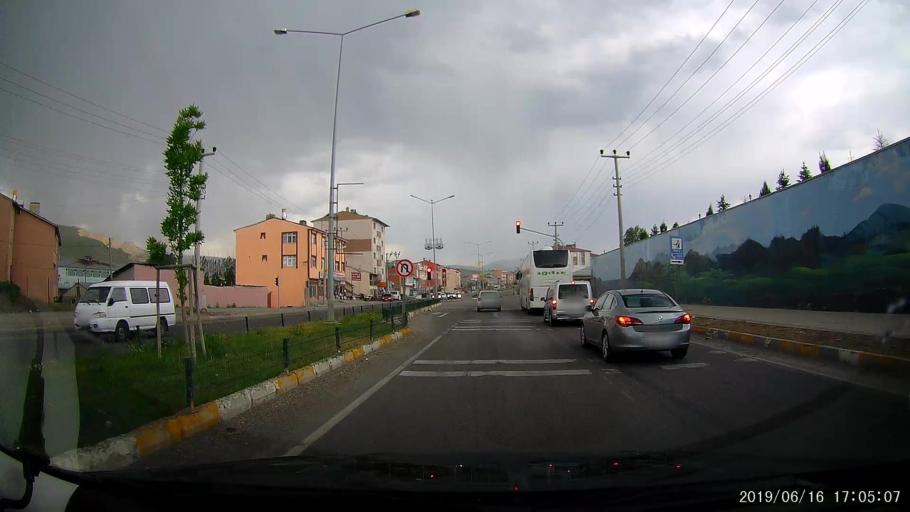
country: TR
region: Erzurum
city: Askale
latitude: 39.9222
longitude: 40.7011
